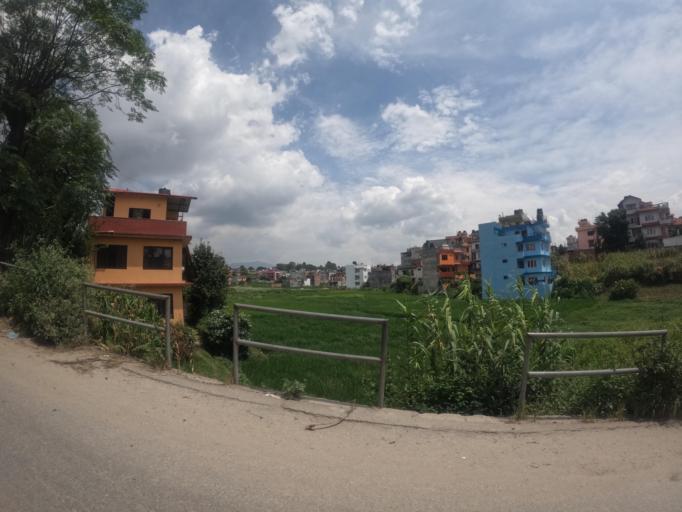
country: NP
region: Central Region
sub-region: Bagmati Zone
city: Kathmandu
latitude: 27.6785
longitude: 85.3660
